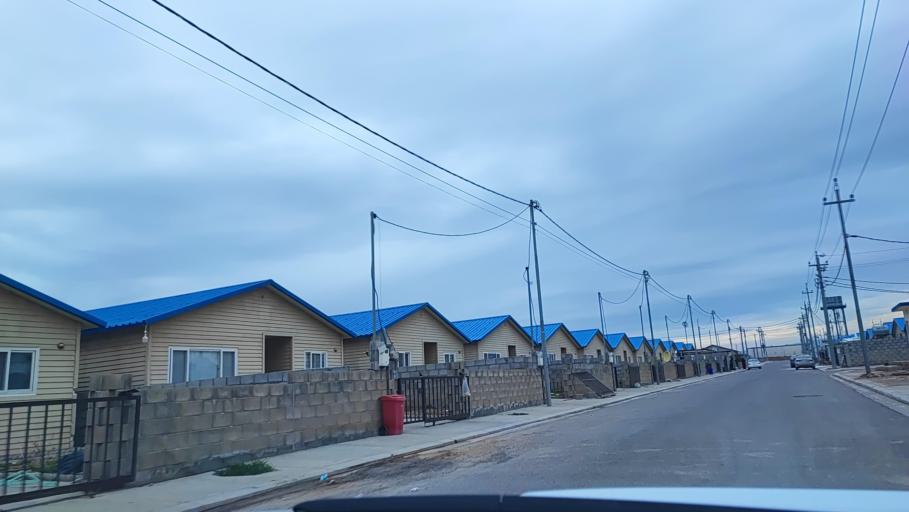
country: IQ
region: Arbil
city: Erbil
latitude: 36.2843
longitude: 44.0830
